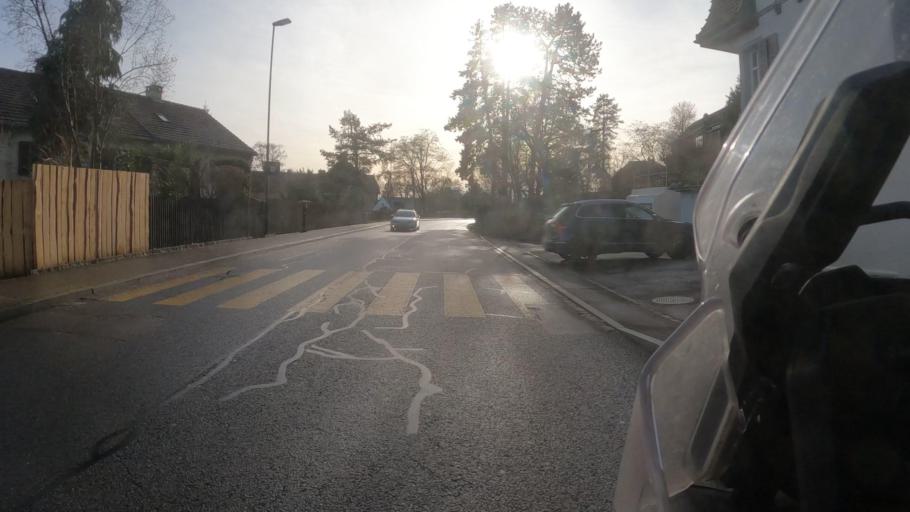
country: CH
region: Schaffhausen
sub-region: Bezirk Schaffhausen
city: Neuhausen
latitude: 47.6871
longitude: 8.6175
